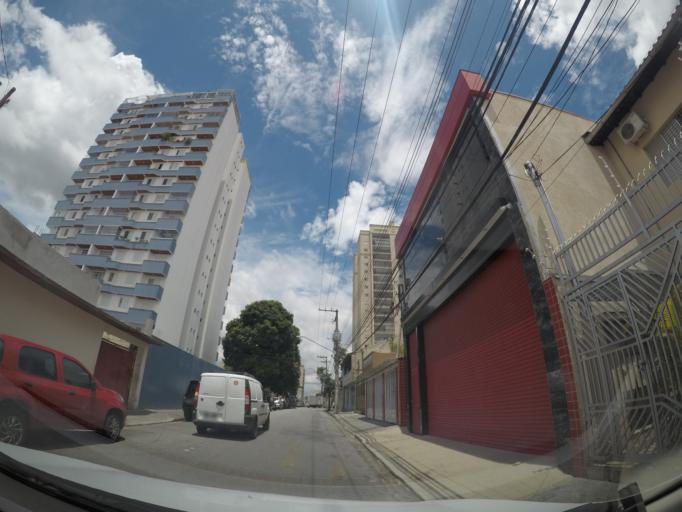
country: BR
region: Sao Paulo
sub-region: Guarulhos
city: Guarulhos
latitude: -23.4644
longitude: -46.5203
